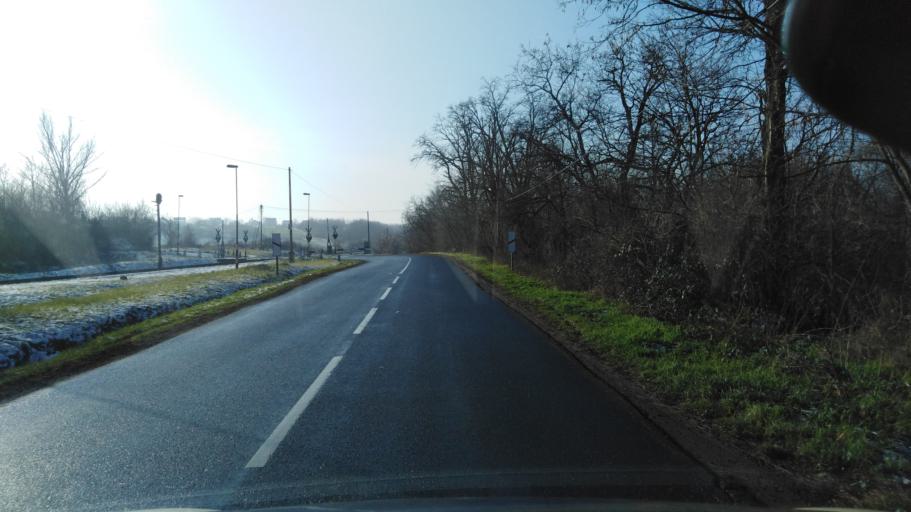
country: HU
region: Nograd
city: Paszto
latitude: 47.9383
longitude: 19.7055
